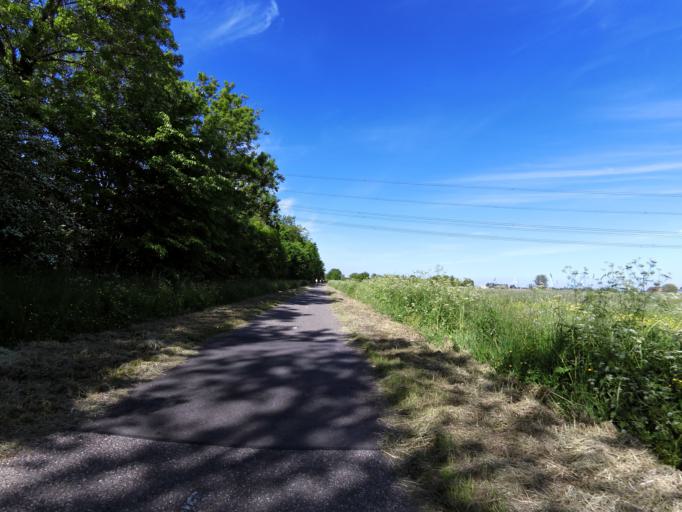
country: NL
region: South Holland
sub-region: Gemeente Brielle
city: Brielle
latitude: 51.8833
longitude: 4.1603
